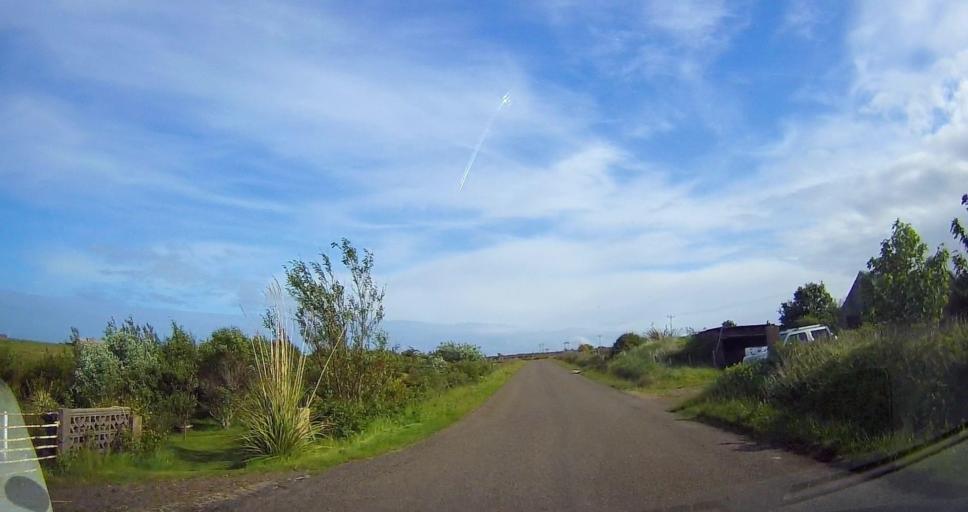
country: GB
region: Scotland
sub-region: Orkney Islands
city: Stromness
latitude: 58.8358
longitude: -3.2142
